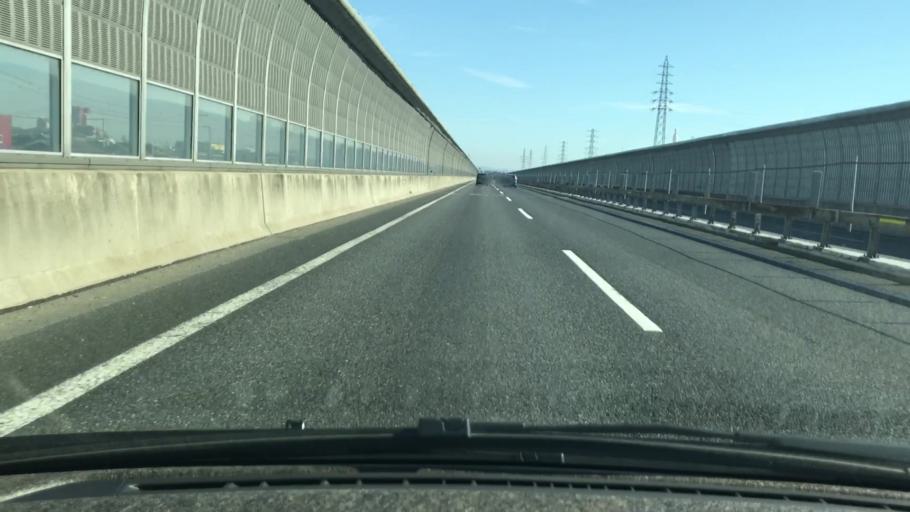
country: JP
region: Hyogo
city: Amagasaki
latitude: 34.7434
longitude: 135.4285
